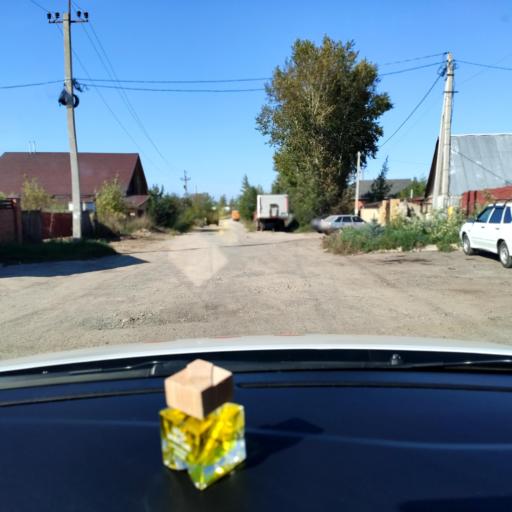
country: RU
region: Tatarstan
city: Vysokaya Gora
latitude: 55.8790
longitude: 49.2484
